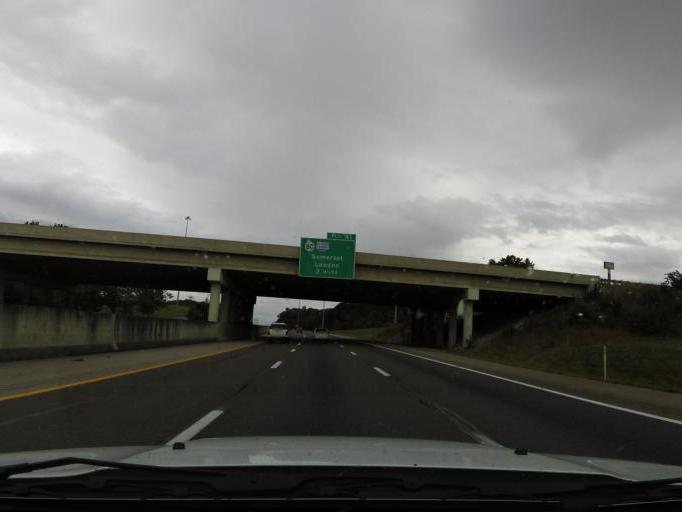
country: US
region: Kentucky
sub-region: Laurel County
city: London
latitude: 37.1099
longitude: -84.1018
